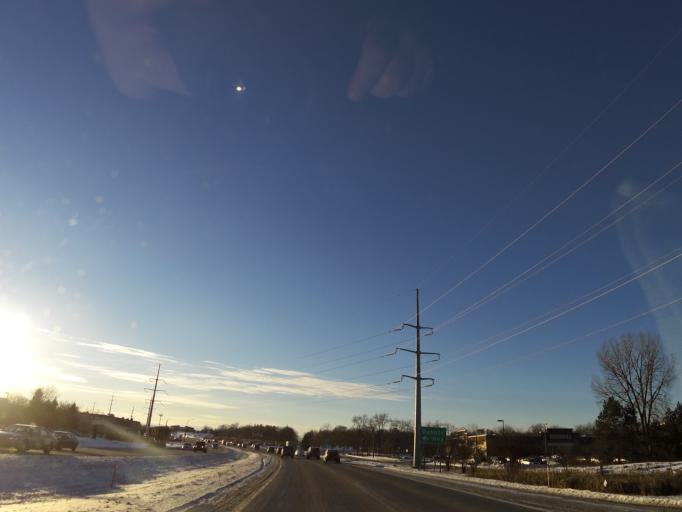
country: US
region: Minnesota
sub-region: Carver County
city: Chanhassen
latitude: 44.8622
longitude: -93.5206
